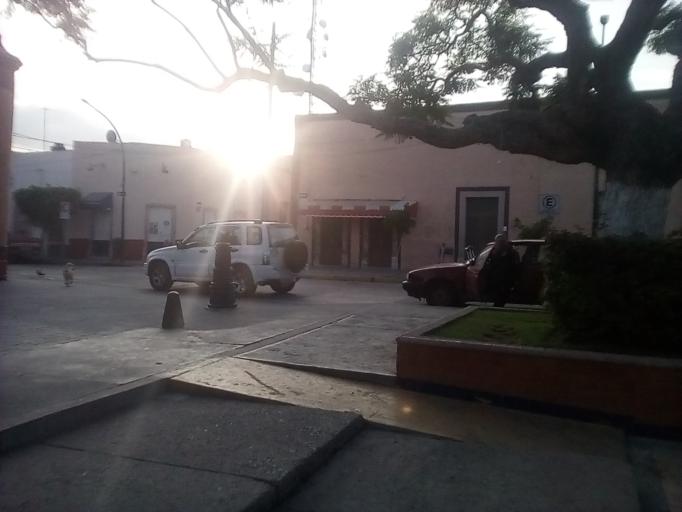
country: MX
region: Guanajuato
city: San Jose Iturbide
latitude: 21.0005
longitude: -100.3852
